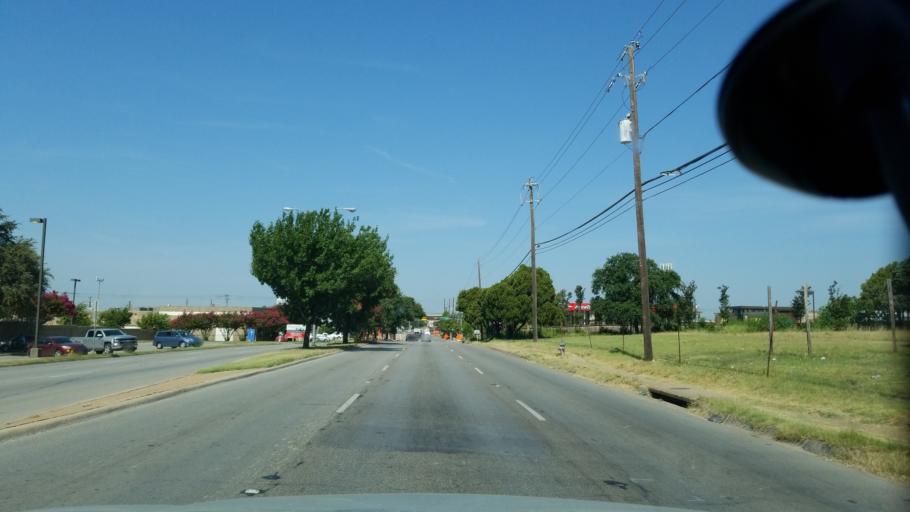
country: US
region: Texas
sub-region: Dallas County
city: Farmers Branch
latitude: 32.8953
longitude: -96.8849
